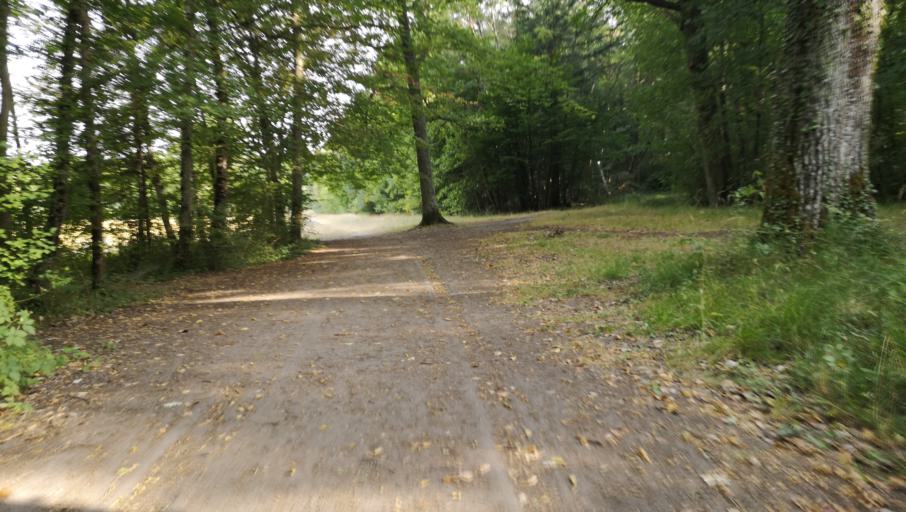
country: FR
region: Centre
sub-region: Departement du Loiret
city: Boigny-sur-Bionne
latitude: 47.9383
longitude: 1.9965
